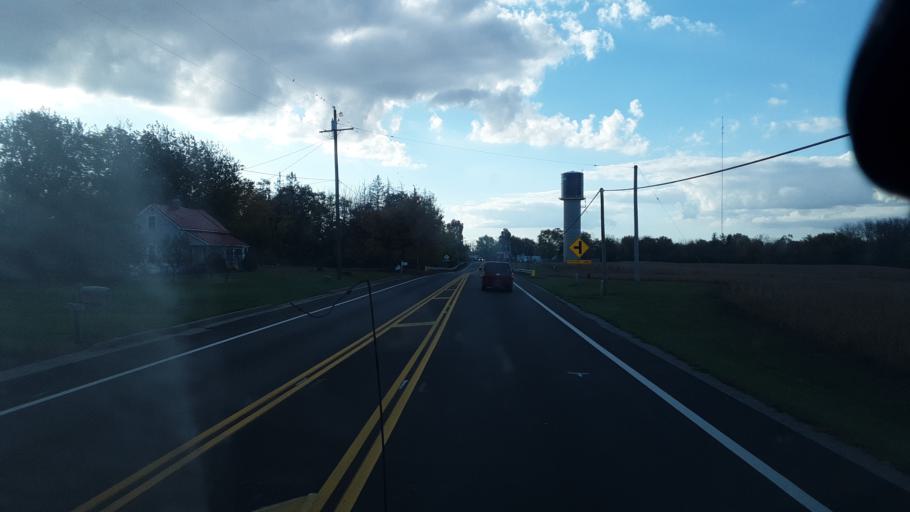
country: US
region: Ohio
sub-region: Fayette County
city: Washington Court House
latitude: 39.5545
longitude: -83.4519
